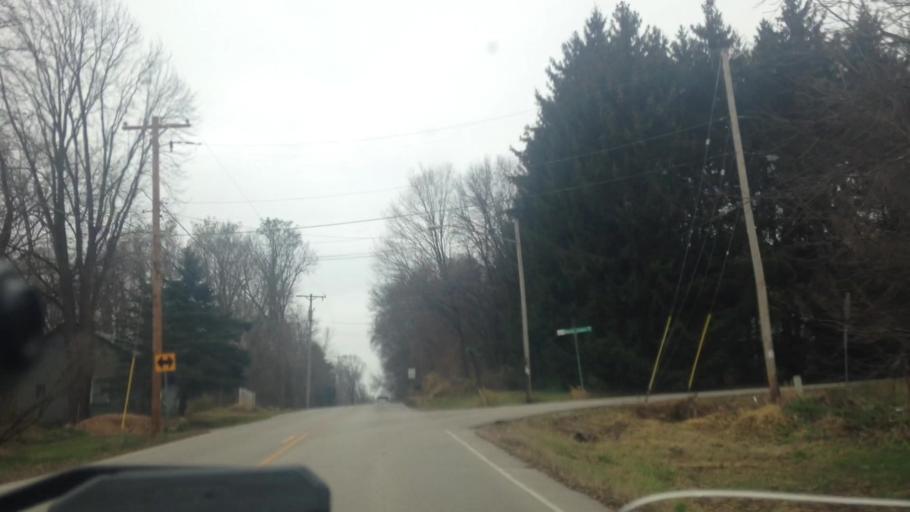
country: US
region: Wisconsin
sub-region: Waukesha County
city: Lannon
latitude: 43.1774
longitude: -88.1829
